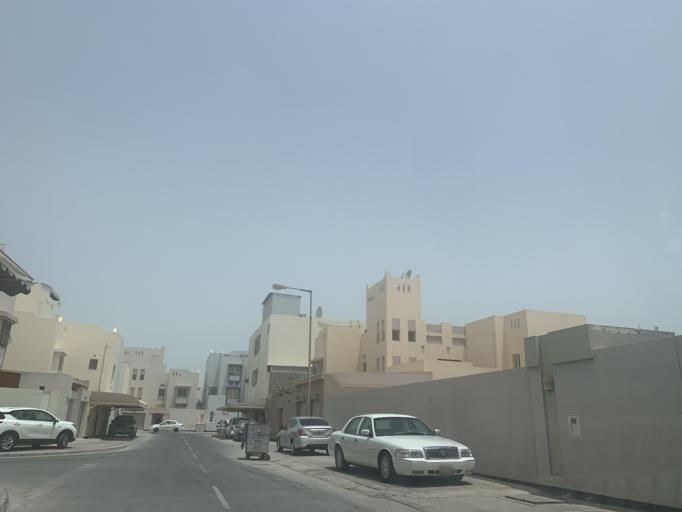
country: BH
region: Manama
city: Jidd Hafs
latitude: 26.2112
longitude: 50.5383
